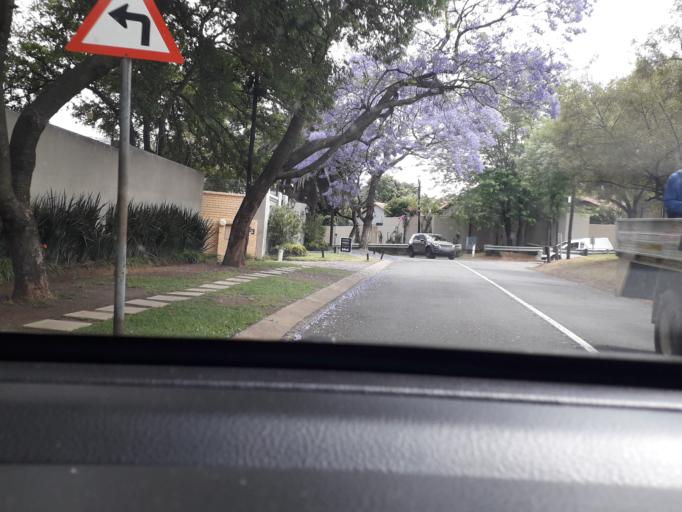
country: ZA
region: Gauteng
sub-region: City of Johannesburg Metropolitan Municipality
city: Modderfontein
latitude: -26.0809
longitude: 28.0584
